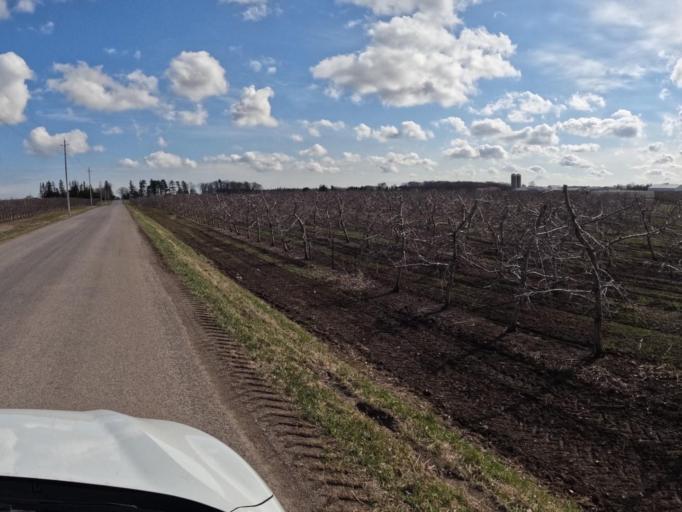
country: CA
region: Ontario
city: Norfolk County
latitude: 42.8736
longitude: -80.2789
